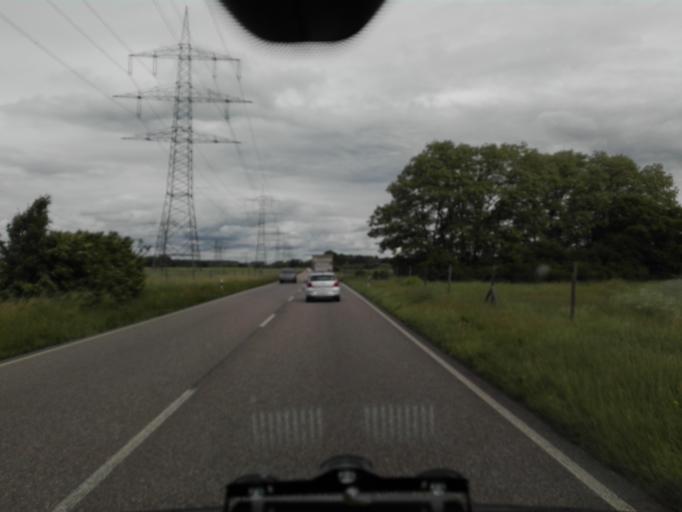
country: DE
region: Baden-Wuerttemberg
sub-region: Karlsruhe Region
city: Linkenheim-Hochstetten
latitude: 49.1329
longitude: 8.4323
